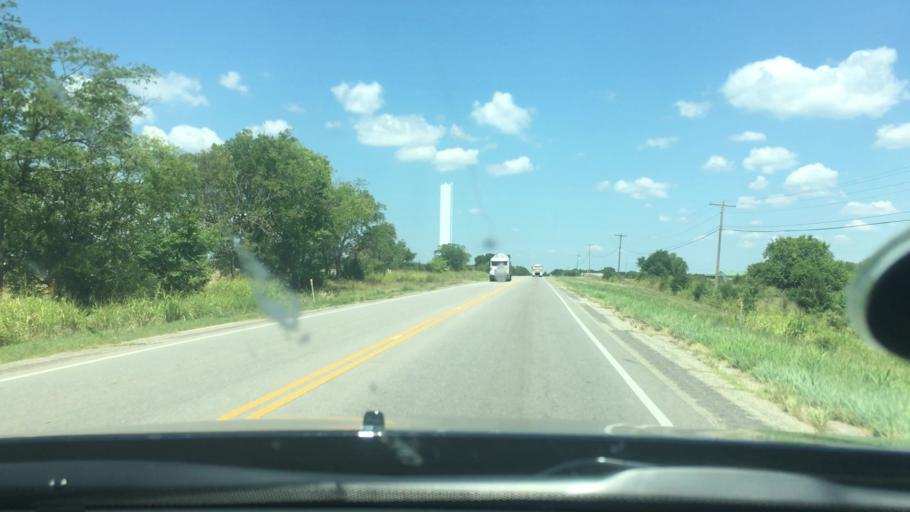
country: US
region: Oklahoma
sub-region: Marshall County
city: Oakland
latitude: 34.1369
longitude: -96.7982
